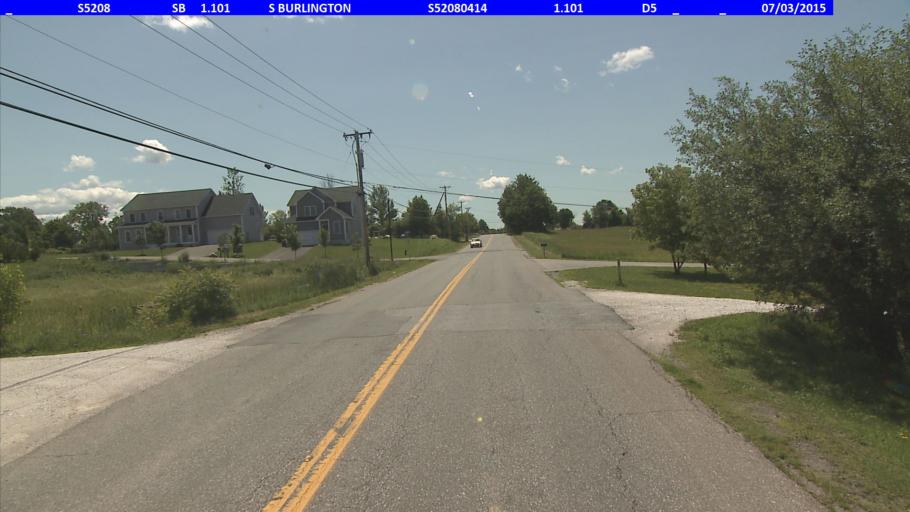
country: US
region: Vermont
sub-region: Chittenden County
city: South Burlington
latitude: 44.4266
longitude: -73.1744
